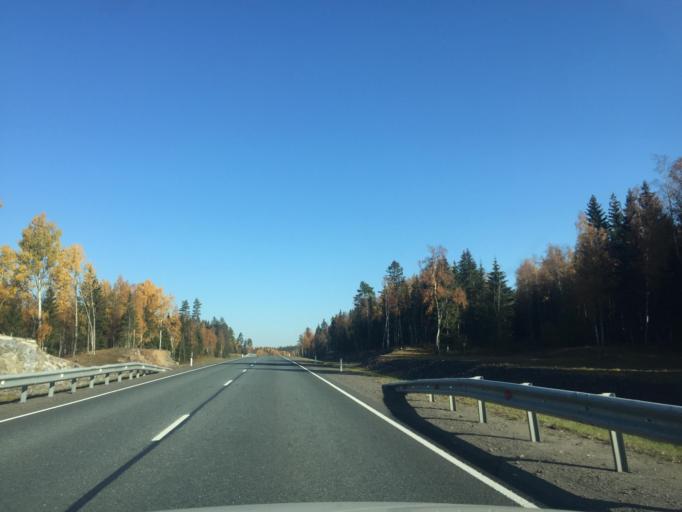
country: RU
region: Leningrad
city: Kuznechnoye
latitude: 61.3560
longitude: 29.8877
